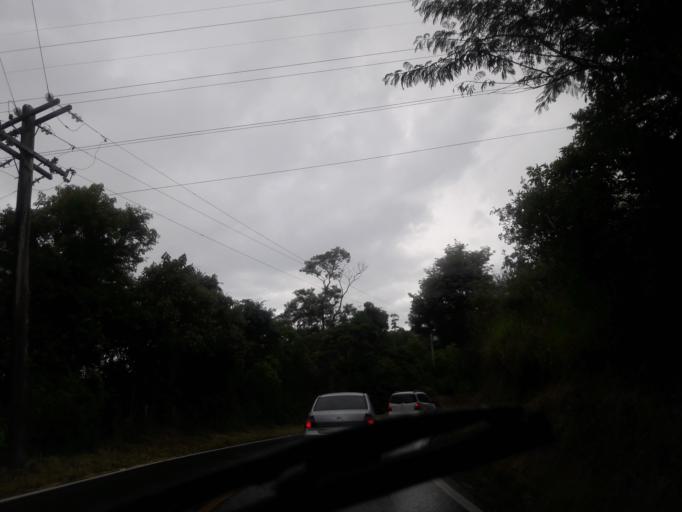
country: BR
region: Sao Paulo
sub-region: Aruja
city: Aruja
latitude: -23.3255
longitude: -46.4323
